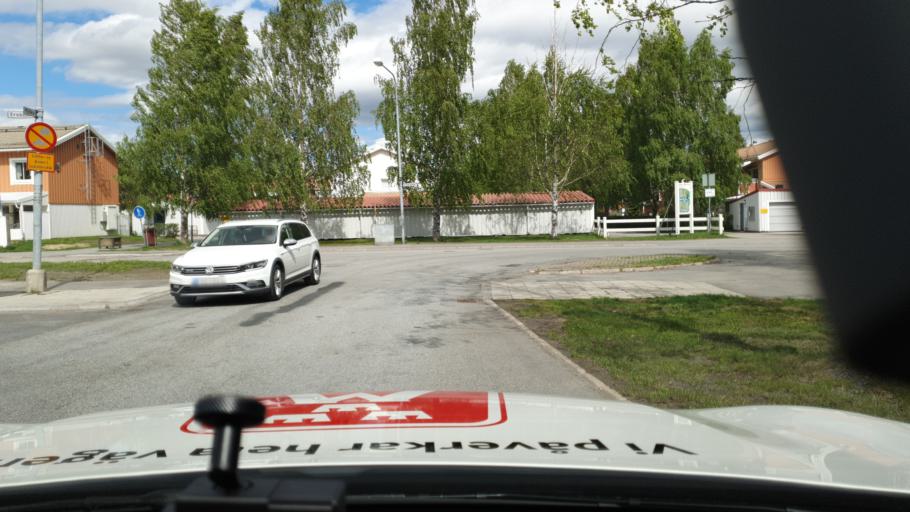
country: SE
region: Vaesterbotten
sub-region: Umea Kommun
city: Ersmark
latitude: 63.8634
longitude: 20.3382
